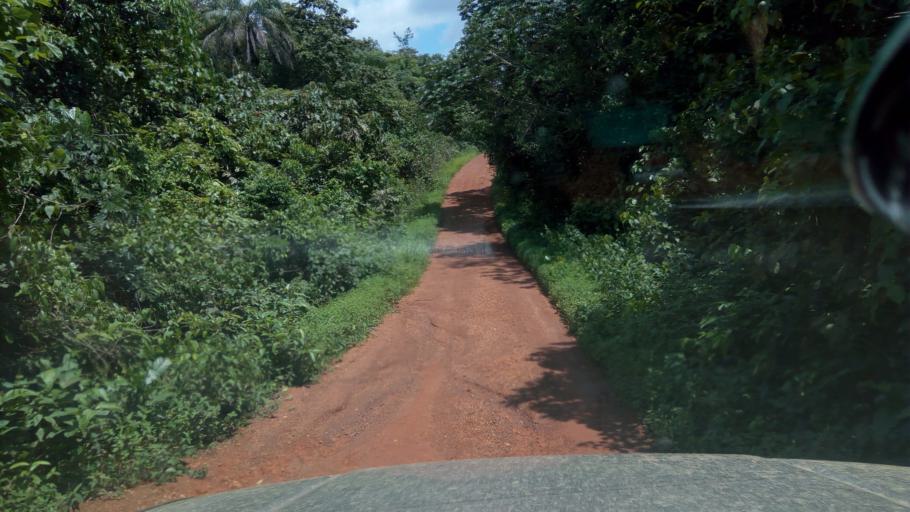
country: SL
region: Southern Province
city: Zimmi
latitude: 7.2727
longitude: -11.2575
